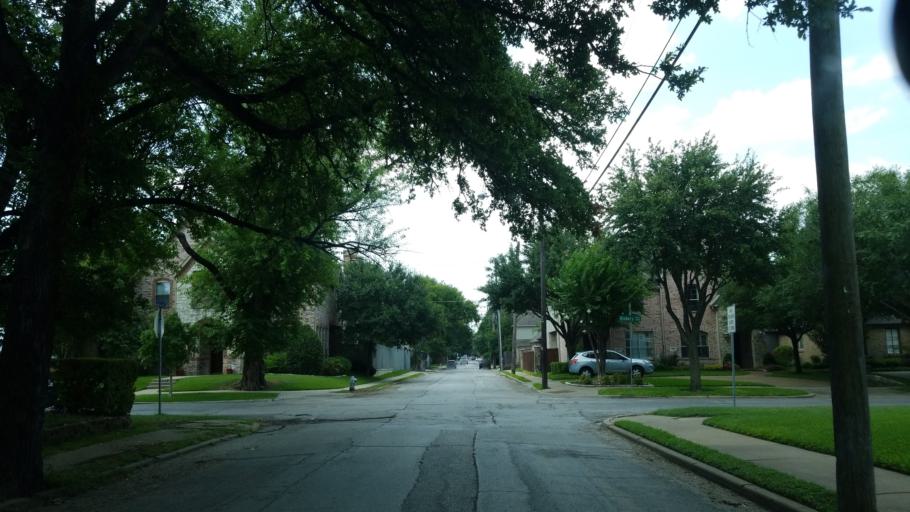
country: US
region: Texas
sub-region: Dallas County
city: Highland Park
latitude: 32.8226
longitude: -96.7824
